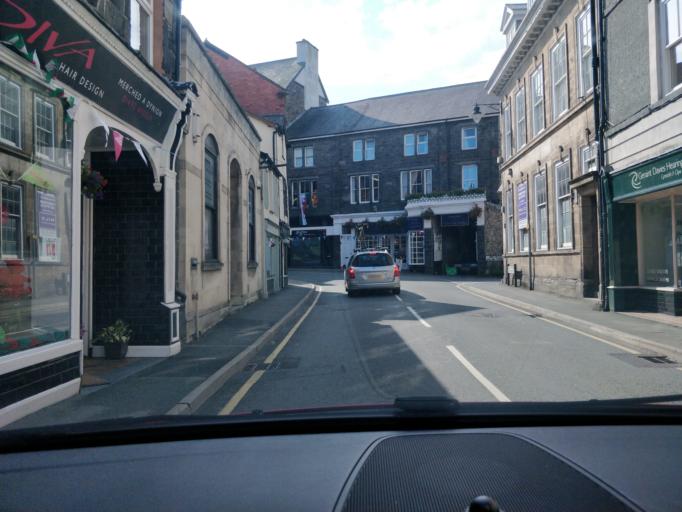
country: GB
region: Wales
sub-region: Conwy
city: Llanrwst
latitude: 53.1388
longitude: -3.7991
